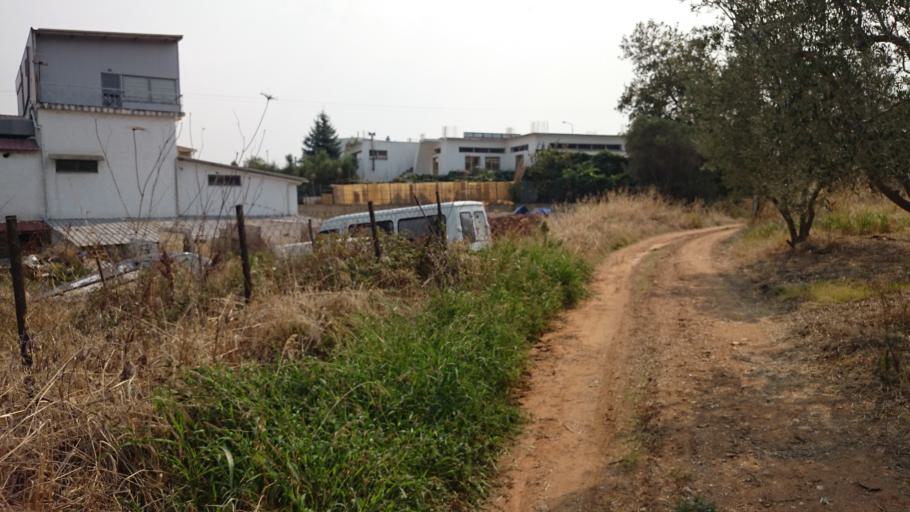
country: GR
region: Central Macedonia
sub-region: Nomos Chalkidikis
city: Nea Moudhania
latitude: 40.2553
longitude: 23.2748
